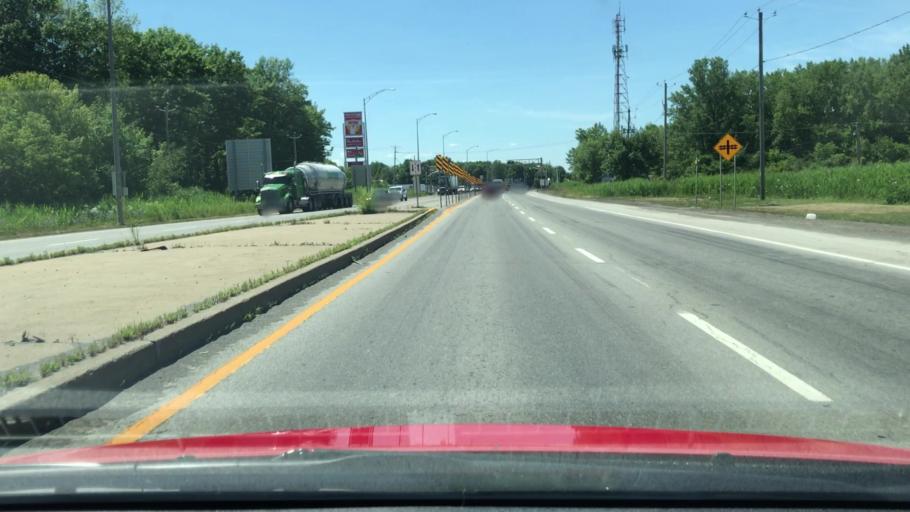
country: CA
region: Quebec
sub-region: Monteregie
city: Saint-Constant
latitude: 45.3955
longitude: -73.6047
